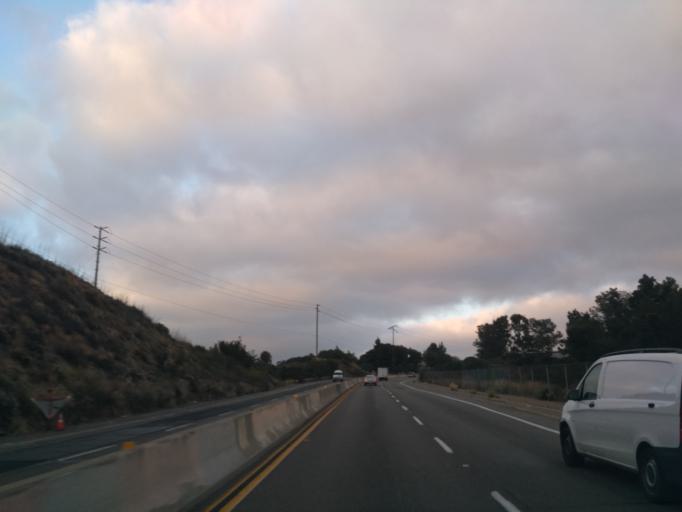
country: US
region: California
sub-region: San Diego County
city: La Jolla
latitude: 32.8103
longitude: -117.2058
